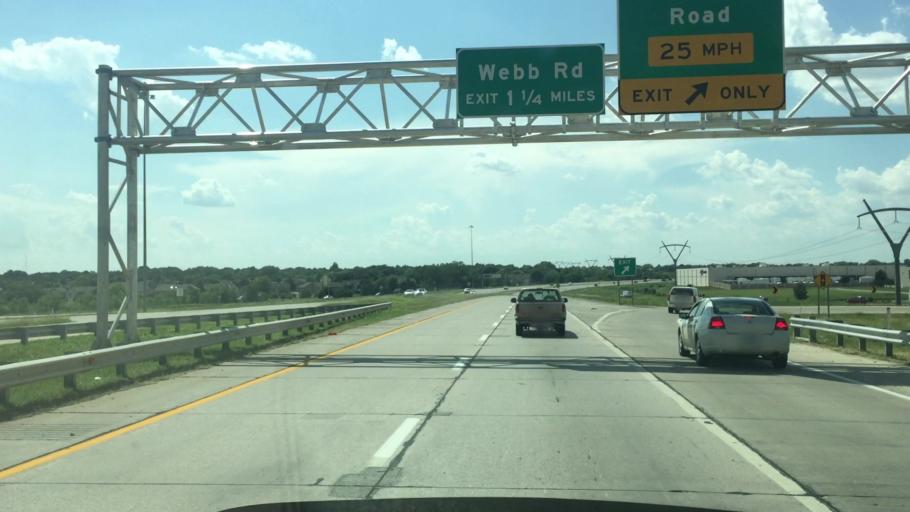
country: US
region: Kansas
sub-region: Sedgwick County
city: Bellaire
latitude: 37.7299
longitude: -97.2084
